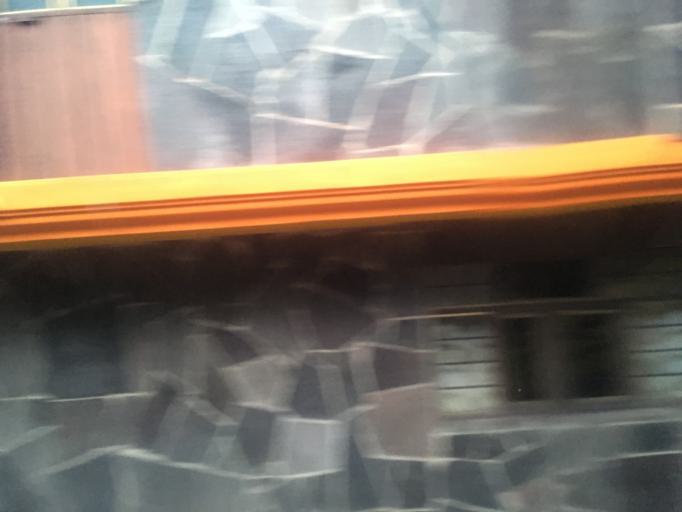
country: MX
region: Puebla
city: Chignahuapan
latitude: 19.8425
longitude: -98.0288
